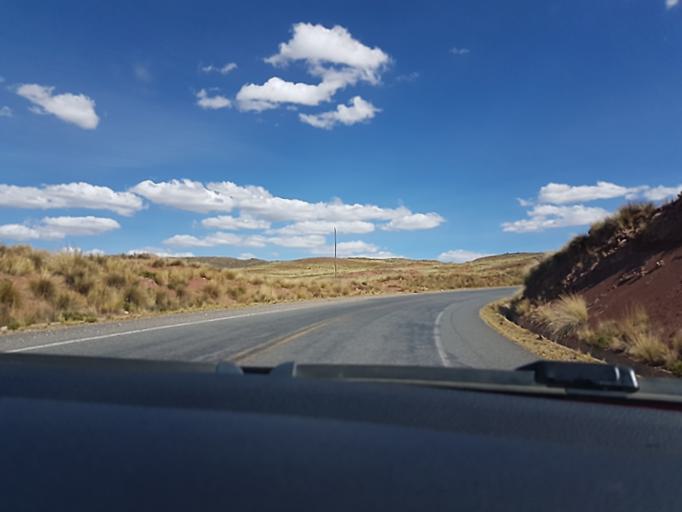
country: BO
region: La Paz
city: Tiahuanaco
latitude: -17.0070
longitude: -68.4270
